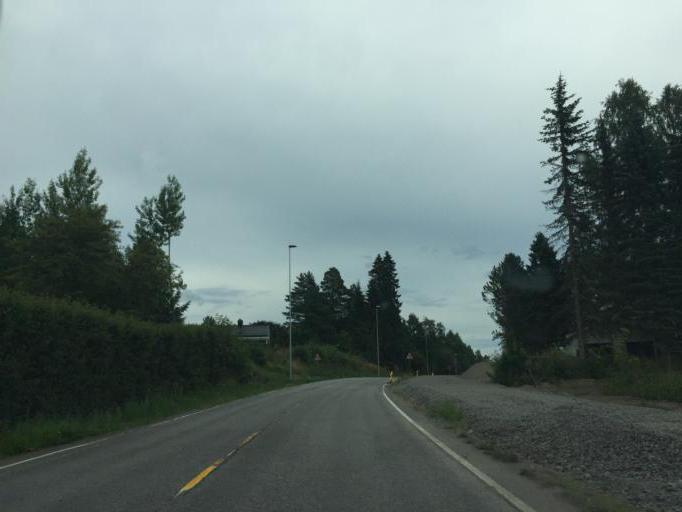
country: NO
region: Hedmark
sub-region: Kongsvinger
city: Kongsvinger
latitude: 60.2002
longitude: 11.9894
